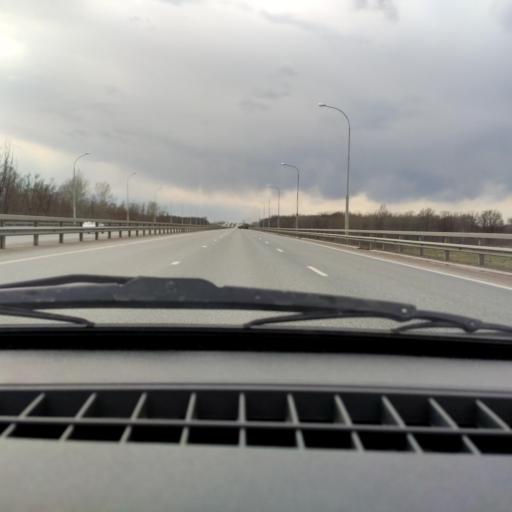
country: RU
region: Bashkortostan
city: Ufa
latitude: 54.6458
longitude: 56.0135
